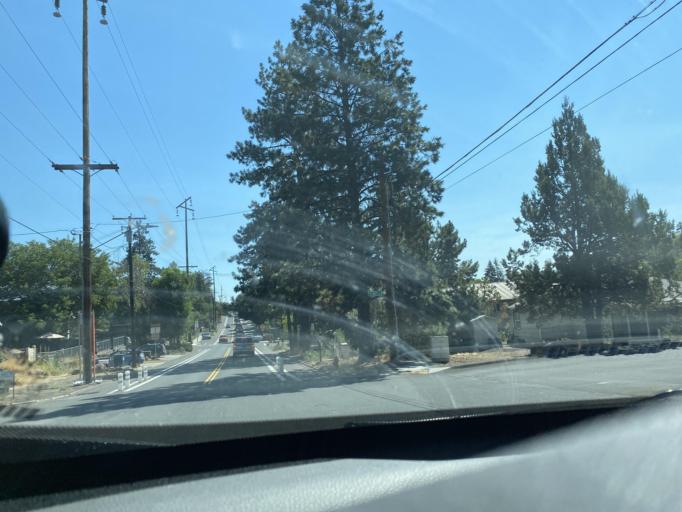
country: US
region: Oregon
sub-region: Deschutes County
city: Bend
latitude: 44.0641
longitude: -121.3290
